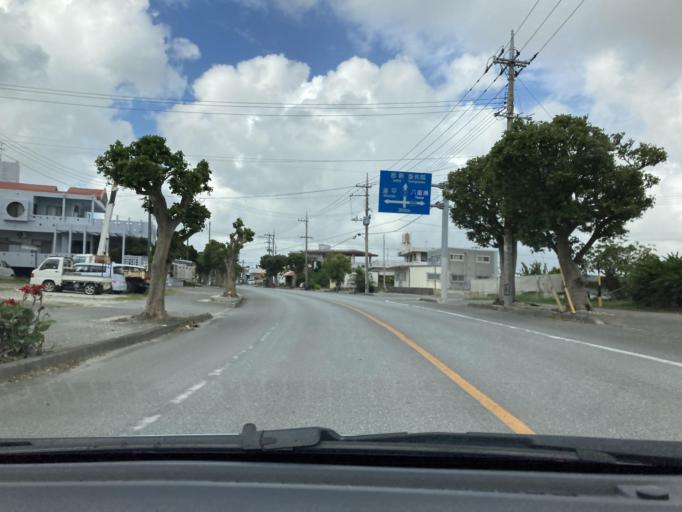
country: JP
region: Okinawa
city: Itoman
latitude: 26.1438
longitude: 127.6936
